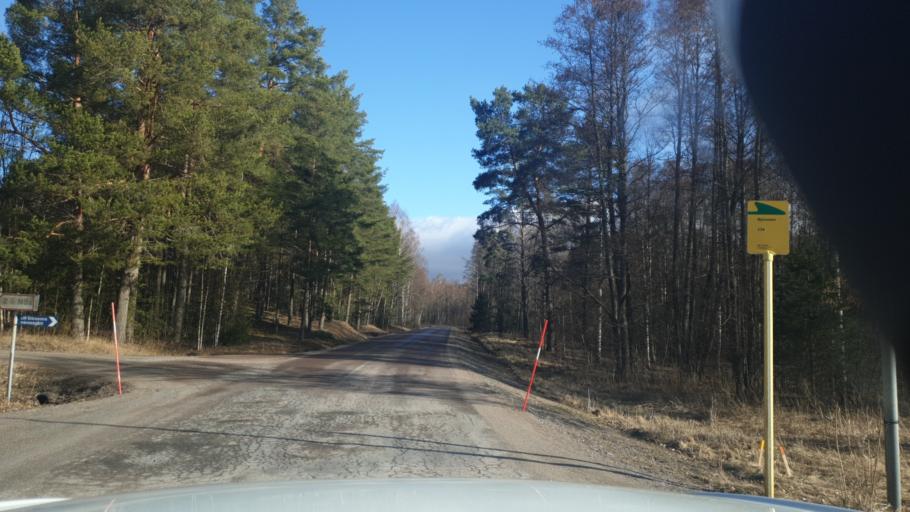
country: SE
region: Vaermland
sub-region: Grums Kommun
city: Slottsbron
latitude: 59.4755
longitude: 12.8837
